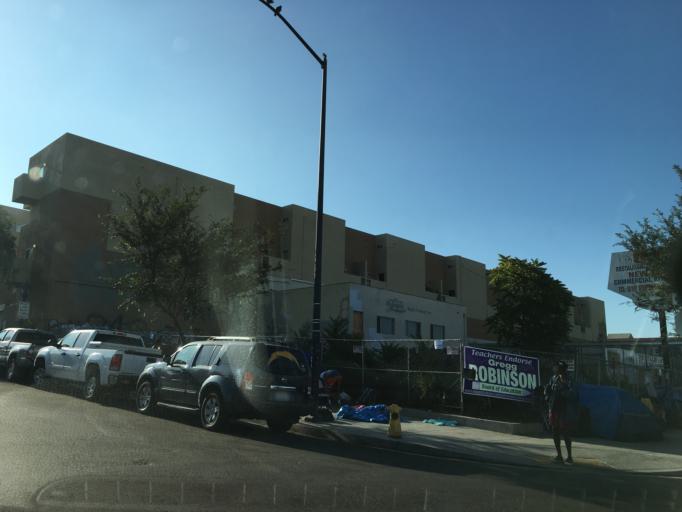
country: US
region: California
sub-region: San Diego County
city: San Diego
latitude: 32.7094
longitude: -117.1494
